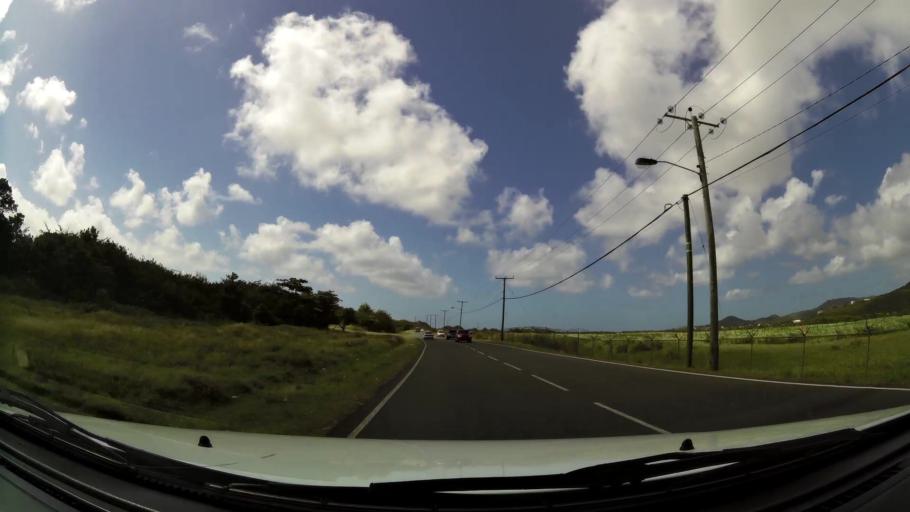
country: LC
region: Vieux-Fort
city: Vieux Fort
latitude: 13.7314
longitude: -60.9575
